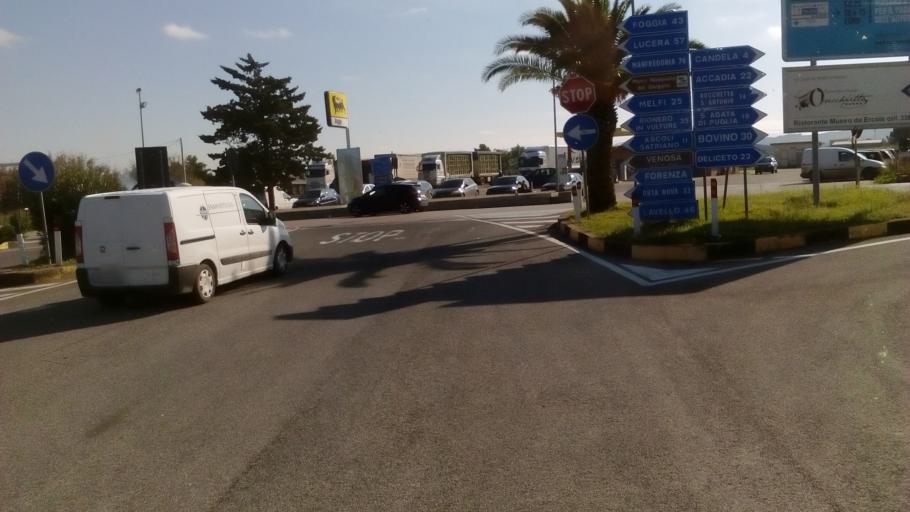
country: IT
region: Apulia
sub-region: Provincia di Foggia
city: Candela
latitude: 41.1505
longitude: 15.5264
